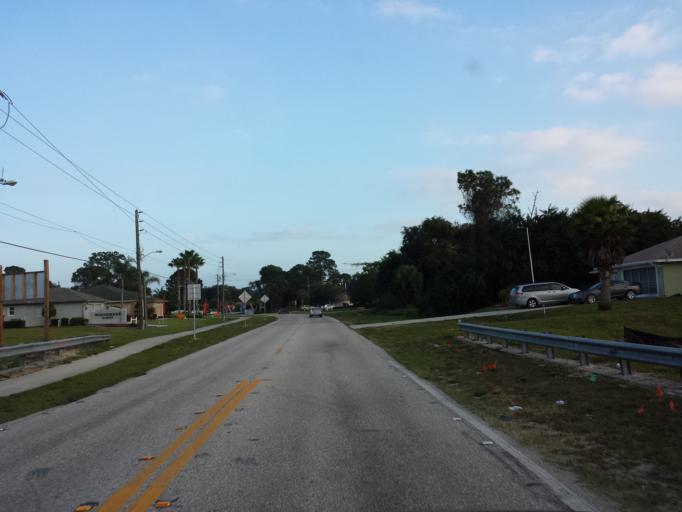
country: US
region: Florida
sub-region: Sarasota County
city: North Port
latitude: 27.0702
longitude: -82.2045
